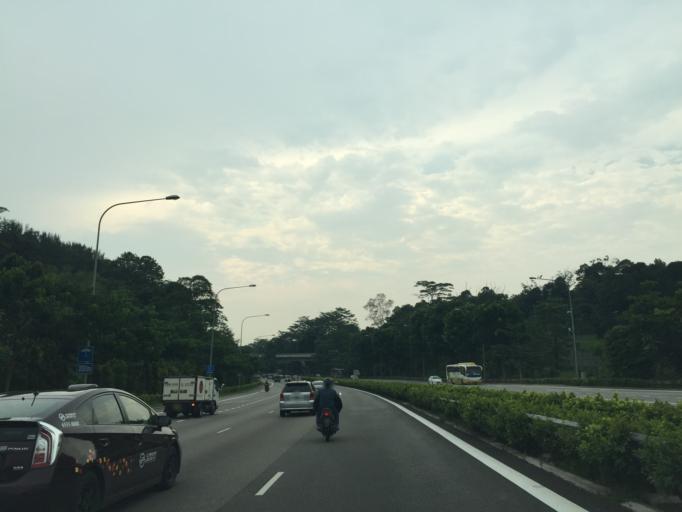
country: SG
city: Singapore
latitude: 1.3514
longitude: 103.7901
